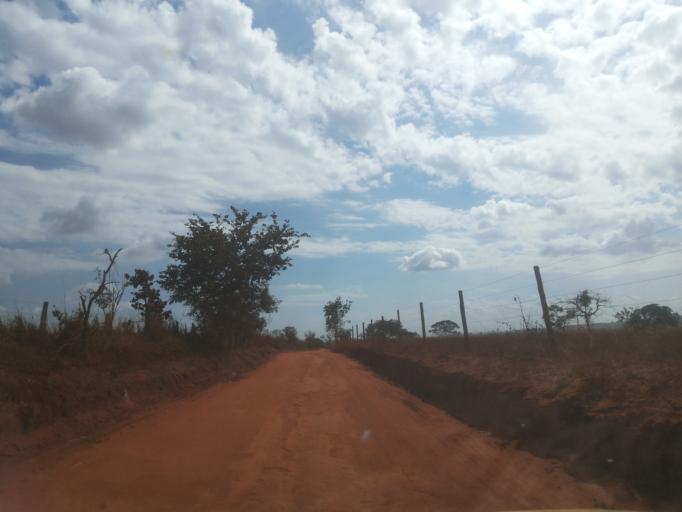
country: BR
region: Minas Gerais
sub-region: Ituiutaba
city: Ituiutaba
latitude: -19.0231
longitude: -49.3945
